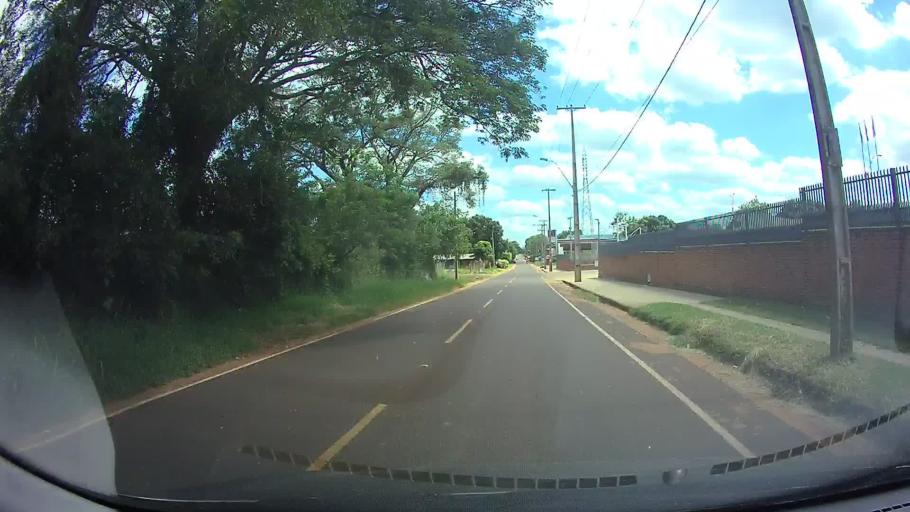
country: PY
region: Central
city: Itaugua
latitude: -25.3801
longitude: -57.3497
